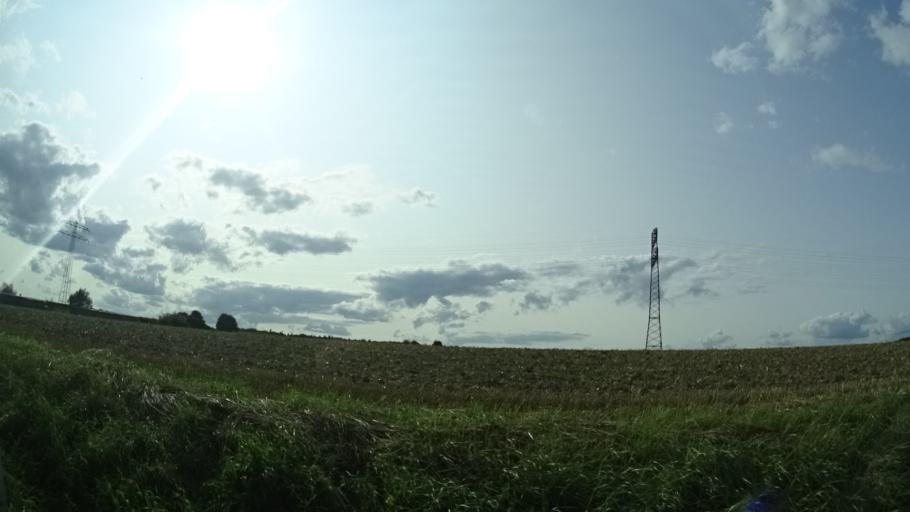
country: DE
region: Baden-Wuerttemberg
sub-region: Karlsruhe Region
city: Hardheim
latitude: 49.6301
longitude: 9.4769
